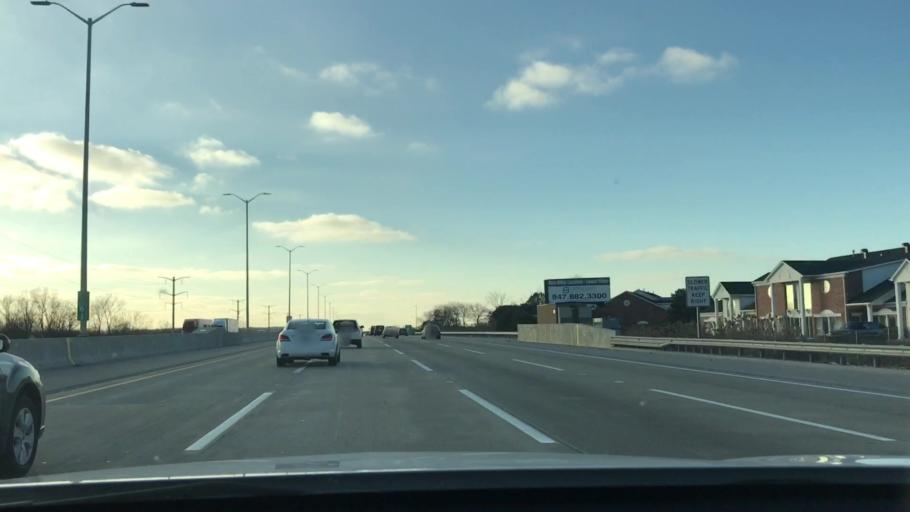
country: US
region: Illinois
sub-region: Cook County
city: Streamwood
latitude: 42.0670
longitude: -88.1673
